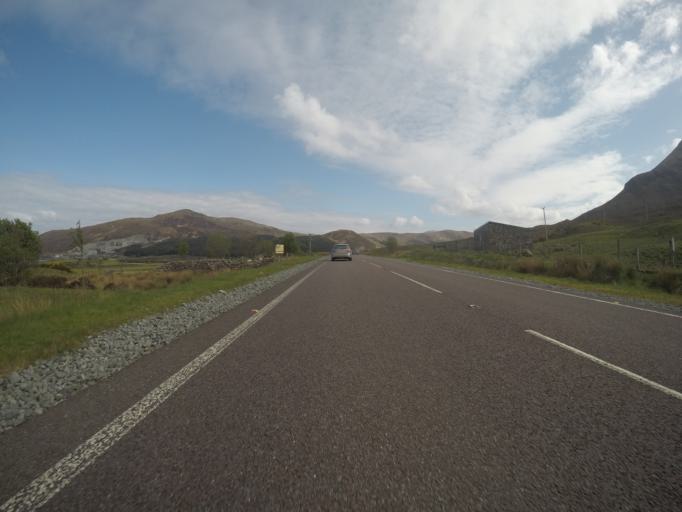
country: GB
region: Scotland
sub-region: Highland
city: Portree
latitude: 57.3106
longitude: -6.0967
